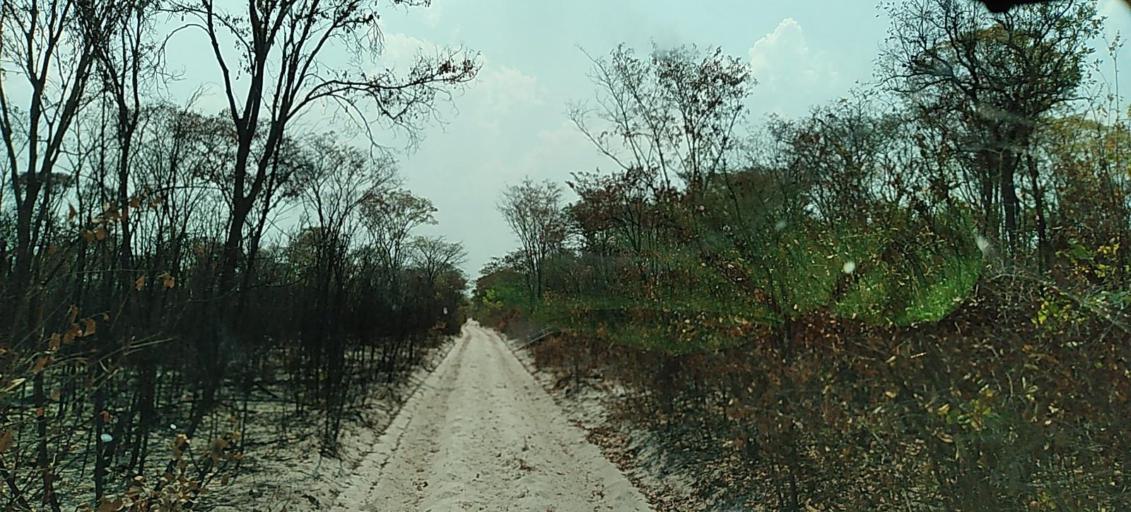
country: ZM
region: North-Western
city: Kabompo
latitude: -13.3923
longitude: 23.7881
